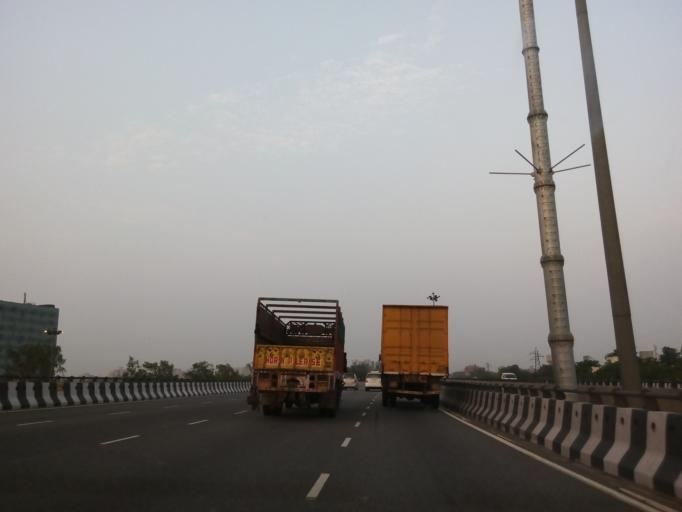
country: IN
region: Haryana
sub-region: Gurgaon
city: Gurgaon
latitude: 28.4792
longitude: 77.0706
